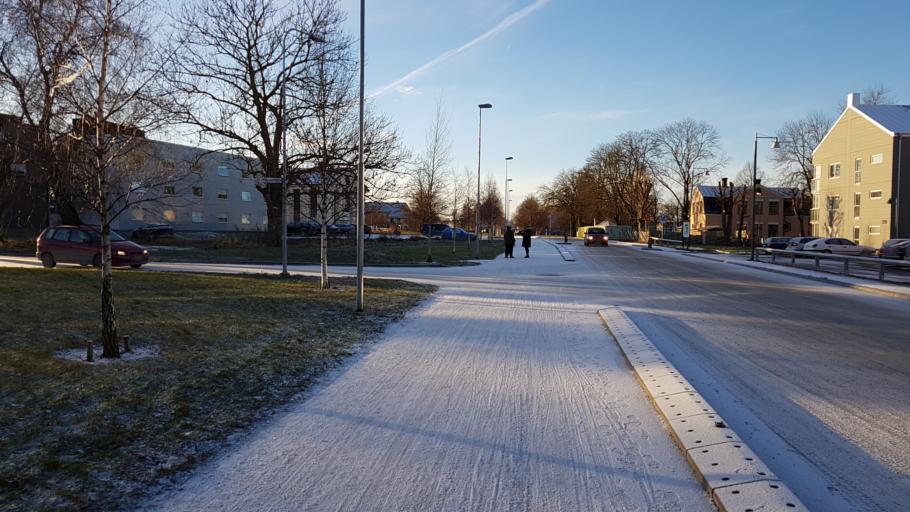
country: SE
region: Gotland
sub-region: Gotland
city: Visby
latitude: 57.6326
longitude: 18.3048
